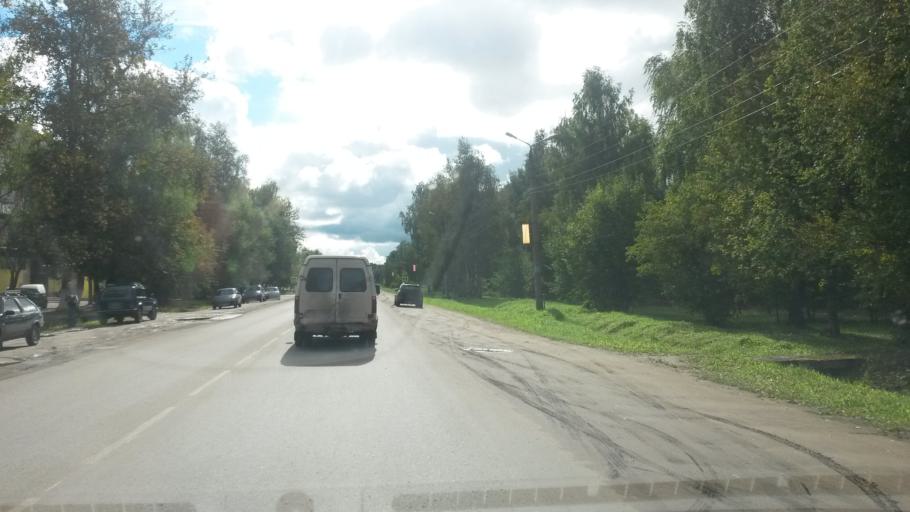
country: RU
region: Ivanovo
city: Zavolzhsk
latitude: 57.4854
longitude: 42.1440
